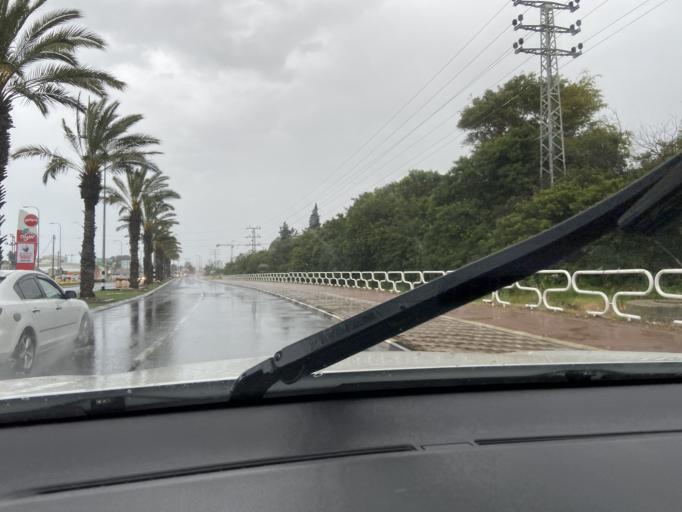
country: IL
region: Northern District
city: El Mazra`a
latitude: 32.9915
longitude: 35.0967
